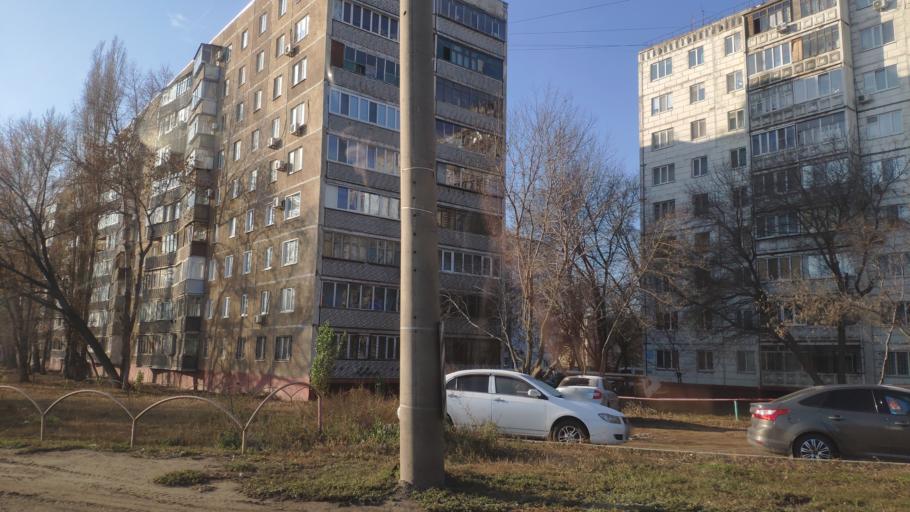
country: RU
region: Orenburg
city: Prigorodnyy
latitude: 51.7769
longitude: 55.1916
